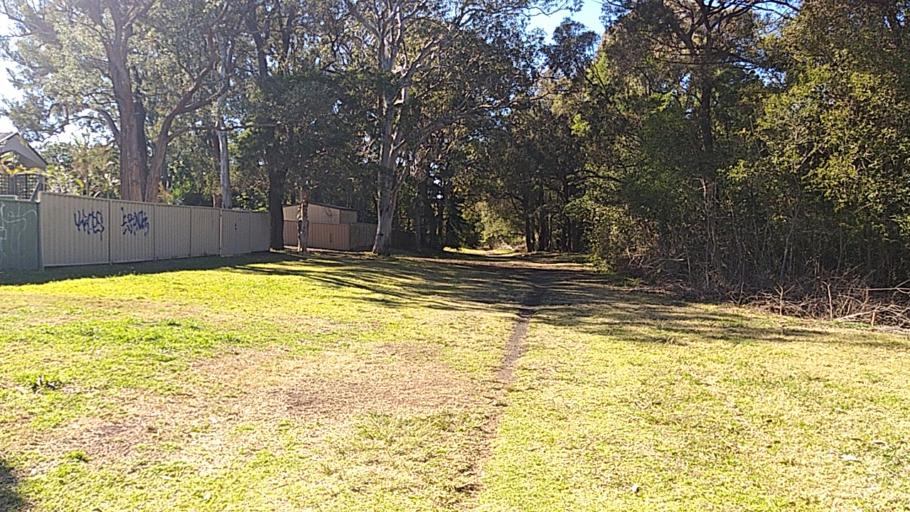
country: AU
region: New South Wales
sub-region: Wollongong
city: Gwynneville
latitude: -34.4191
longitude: 150.8799
